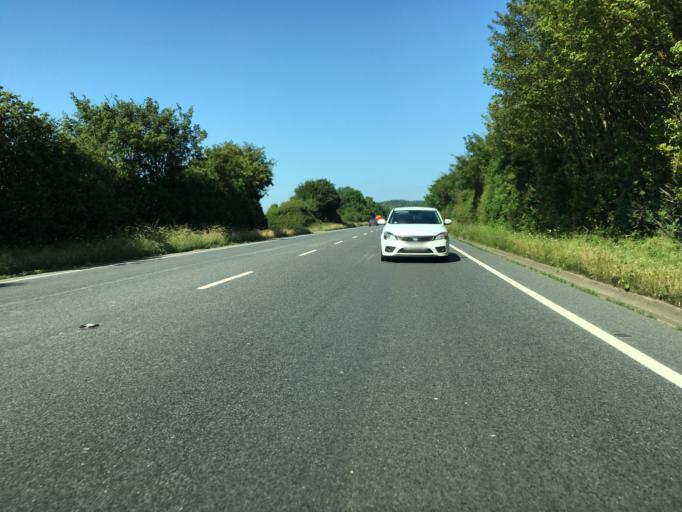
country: GB
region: England
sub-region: Milton Keynes
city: Water Eaton
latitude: 51.9814
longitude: -0.7075
